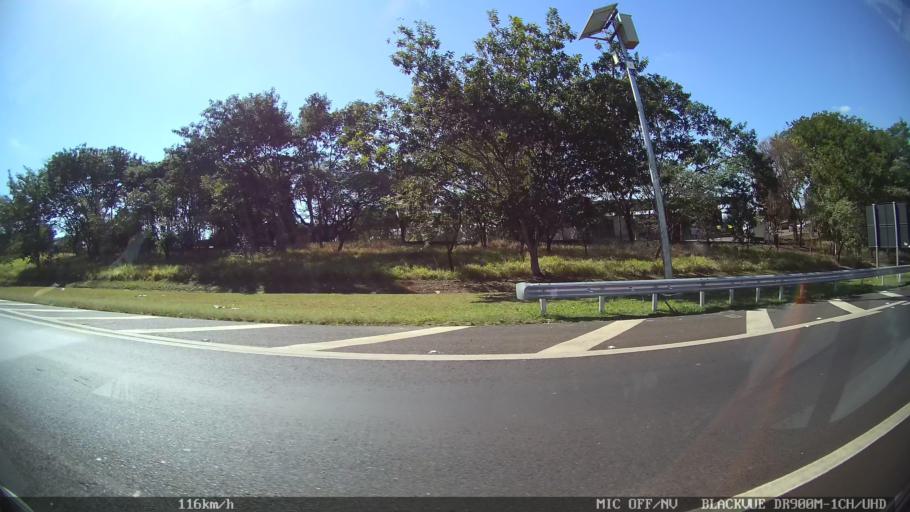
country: BR
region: Sao Paulo
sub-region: Franca
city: Franca
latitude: -20.5498
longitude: -47.4130
